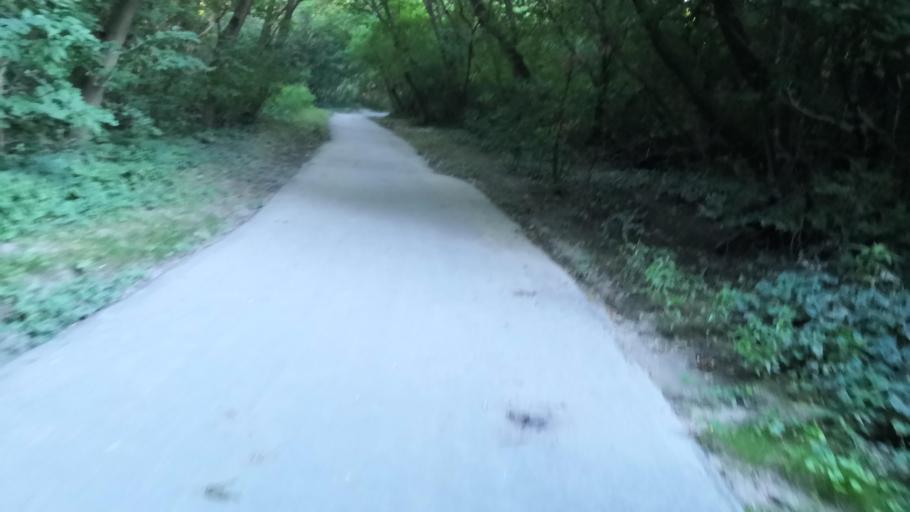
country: CA
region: Ontario
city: Concord
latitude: 43.7901
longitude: -79.4684
